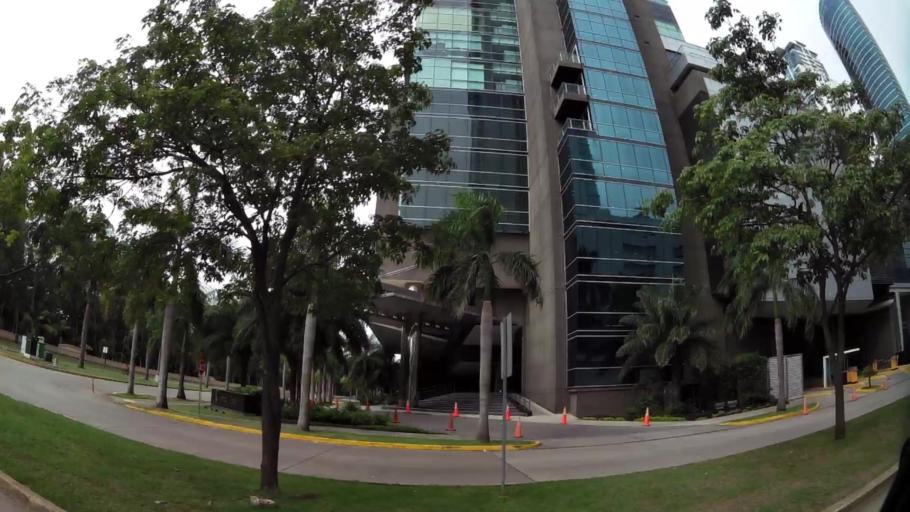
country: PA
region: Panama
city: San Miguelito
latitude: 9.0083
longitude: -79.4756
